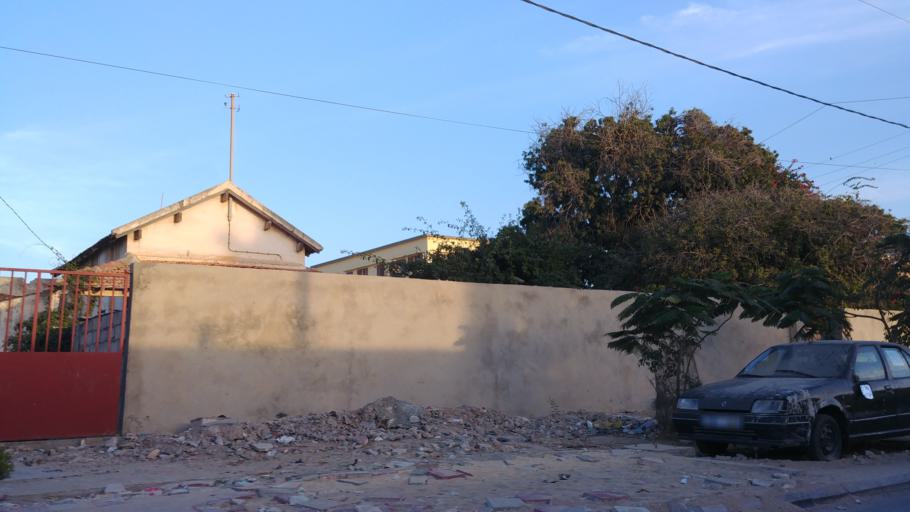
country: SN
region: Saint-Louis
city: Saint-Louis
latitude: 16.0198
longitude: -16.4909
